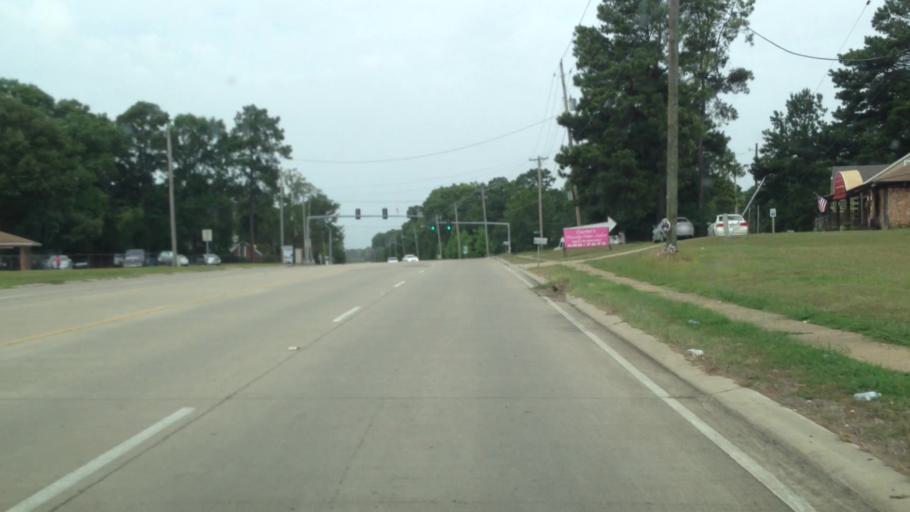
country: US
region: Louisiana
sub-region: De Soto Parish
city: Stonewall
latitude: 32.3952
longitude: -93.8132
